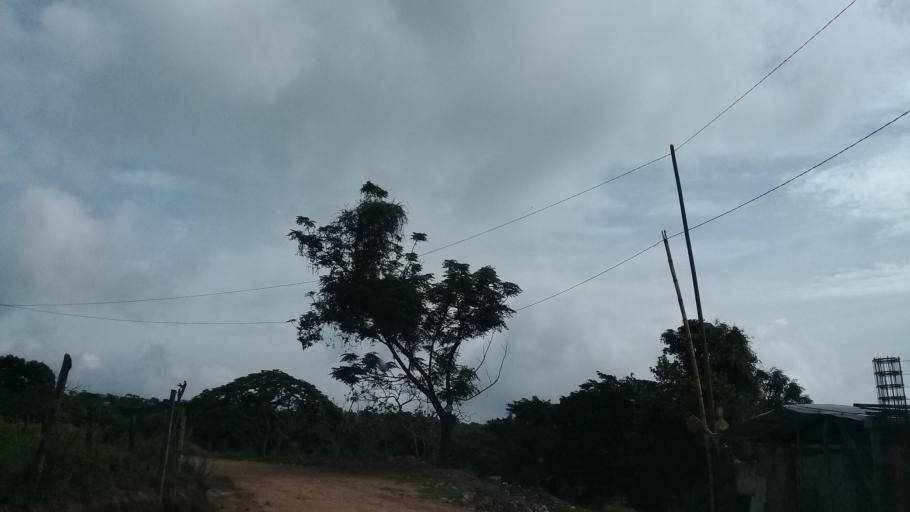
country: MX
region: Veracruz
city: El Castillo
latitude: 19.5525
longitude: -96.8764
